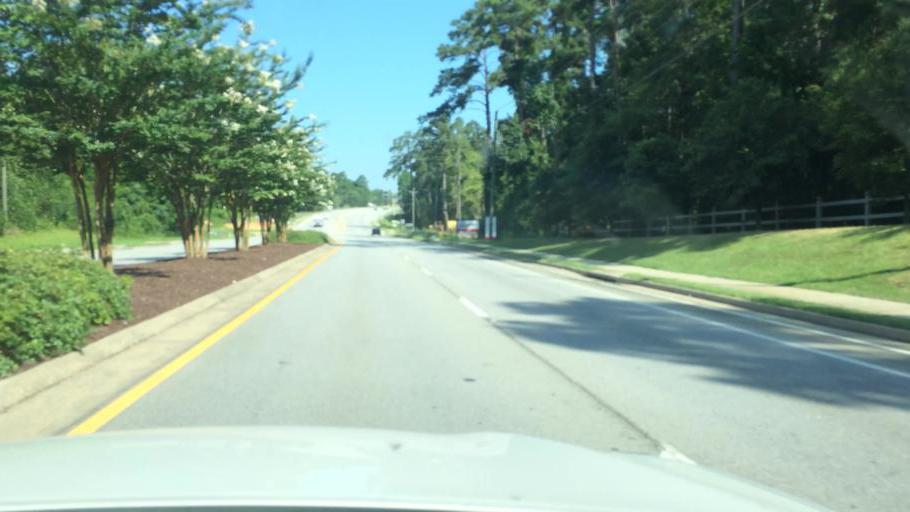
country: US
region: Georgia
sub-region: Columbia County
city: Martinez
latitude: 33.5217
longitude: -82.0651
